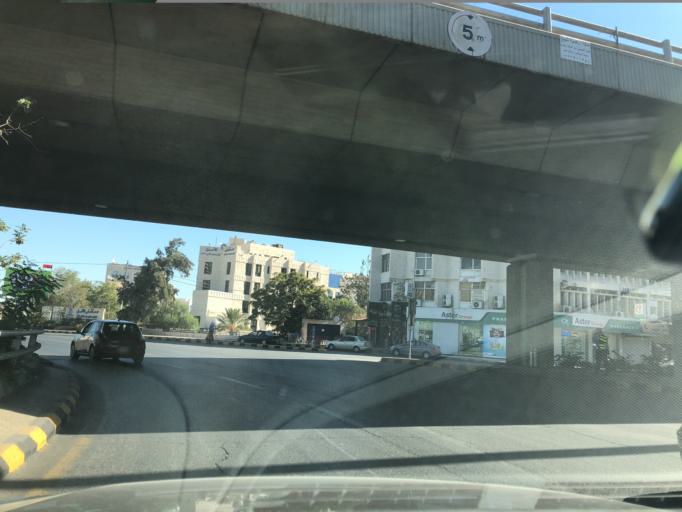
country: JO
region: Amman
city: Amman
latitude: 31.9727
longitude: 35.9100
